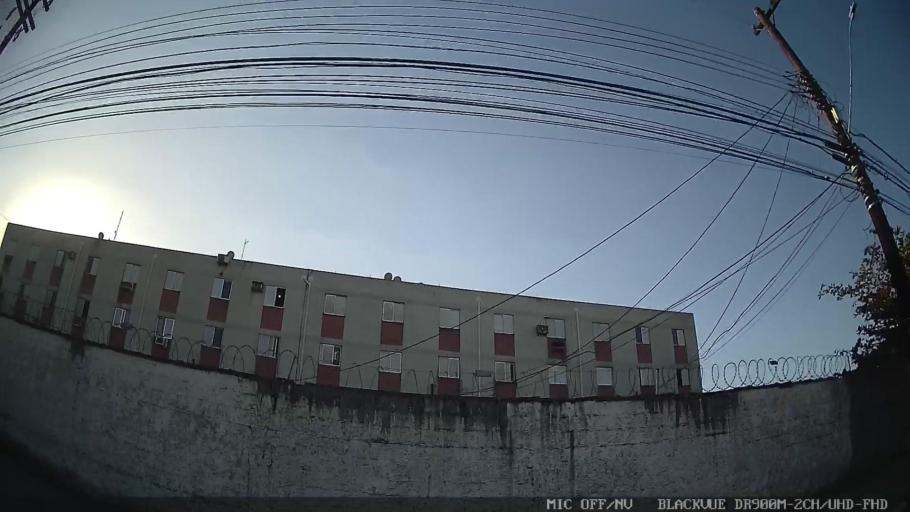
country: BR
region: Sao Paulo
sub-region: Guaruja
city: Guaruja
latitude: -23.9736
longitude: -46.2705
